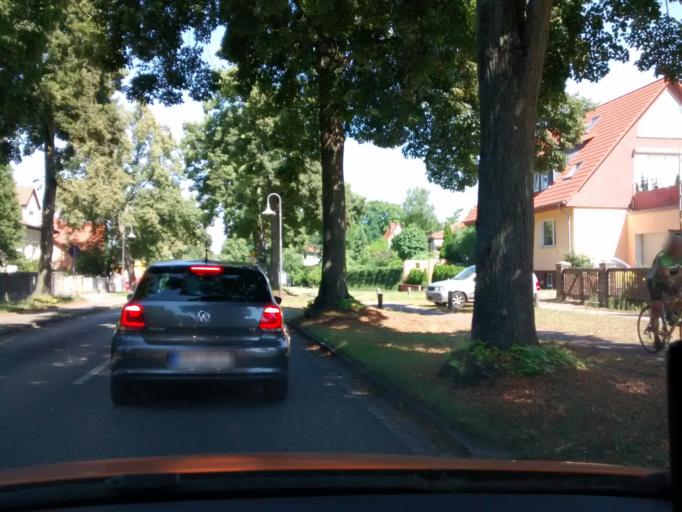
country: DE
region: Brandenburg
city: Birkenwerder
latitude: 52.6852
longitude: 13.2825
